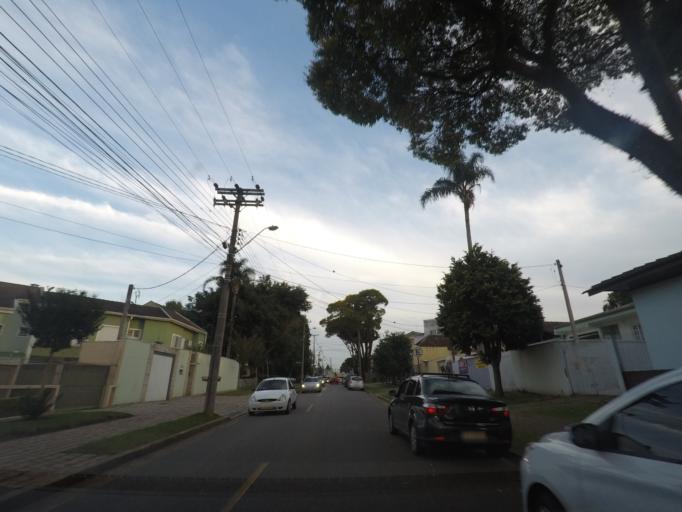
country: BR
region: Parana
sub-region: Curitiba
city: Curitiba
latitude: -25.4179
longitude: -49.2760
